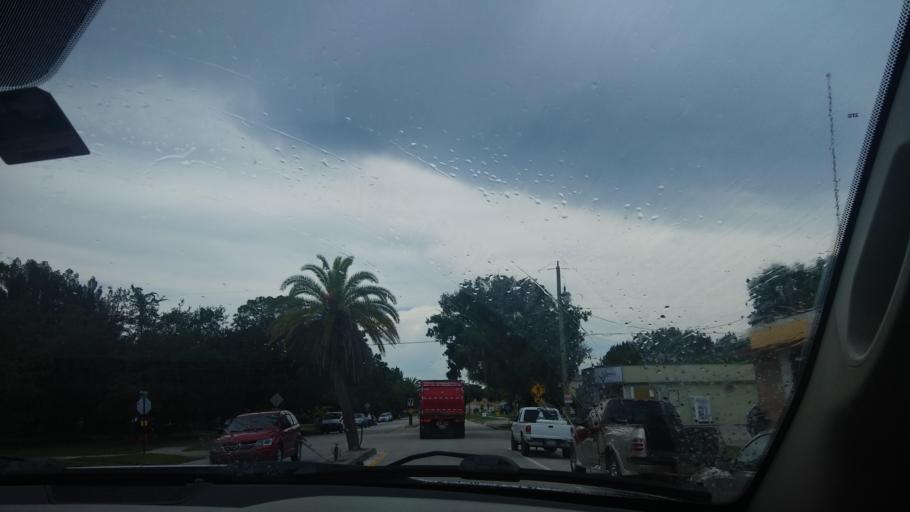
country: US
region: Florida
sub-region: Indian River County
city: Fellsmere
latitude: 27.7721
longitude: -80.6012
